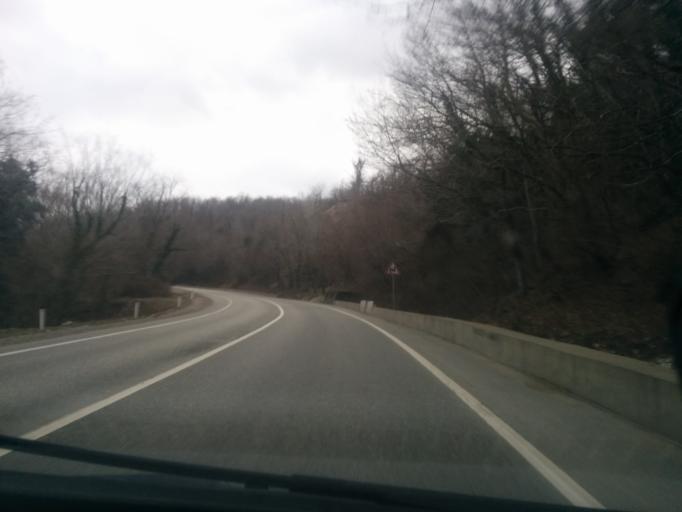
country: RU
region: Krasnodarskiy
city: Novomikhaylovskiy
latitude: 44.2539
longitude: 38.8822
